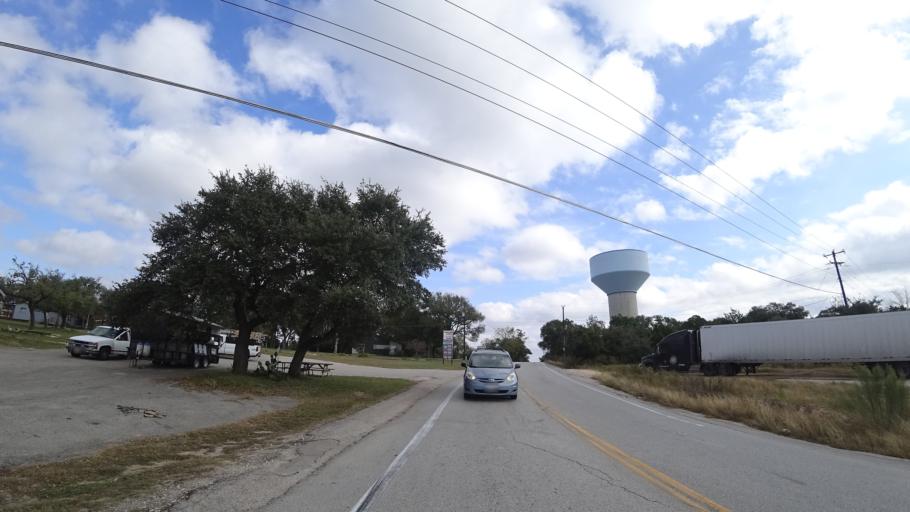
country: US
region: Texas
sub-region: Travis County
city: Bee Cave
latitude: 30.2463
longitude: -97.9271
